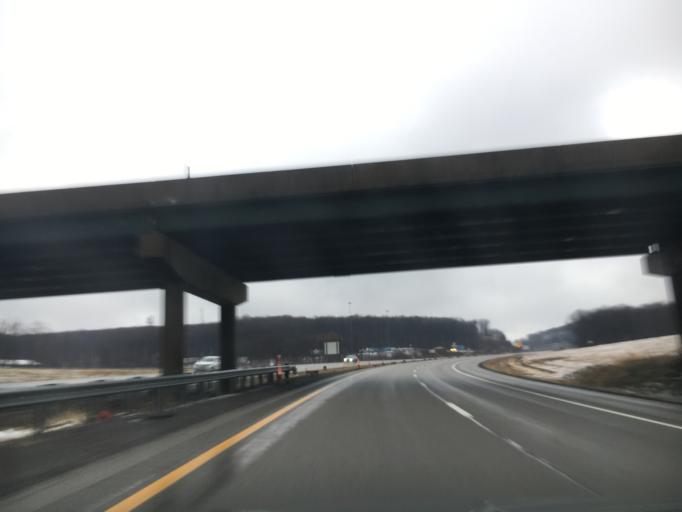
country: US
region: West Virginia
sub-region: Monongalia County
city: Cheat Lake
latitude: 39.6585
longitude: -79.7807
